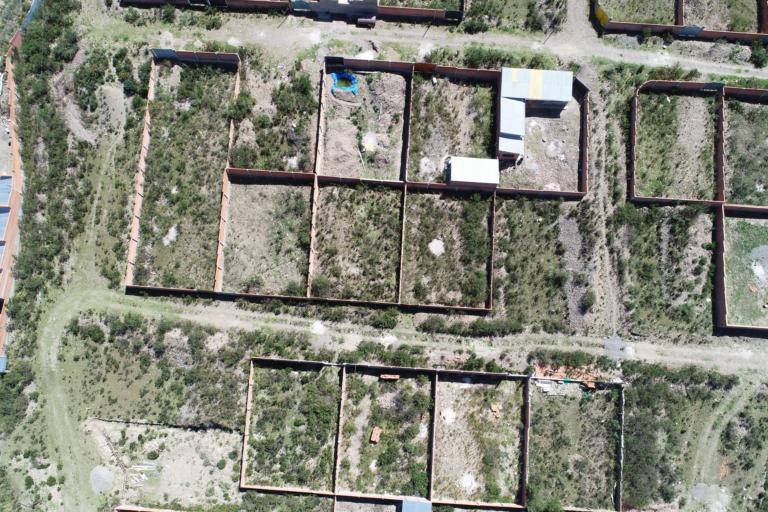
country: BO
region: La Paz
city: La Paz
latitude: -16.5045
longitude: -68.0584
